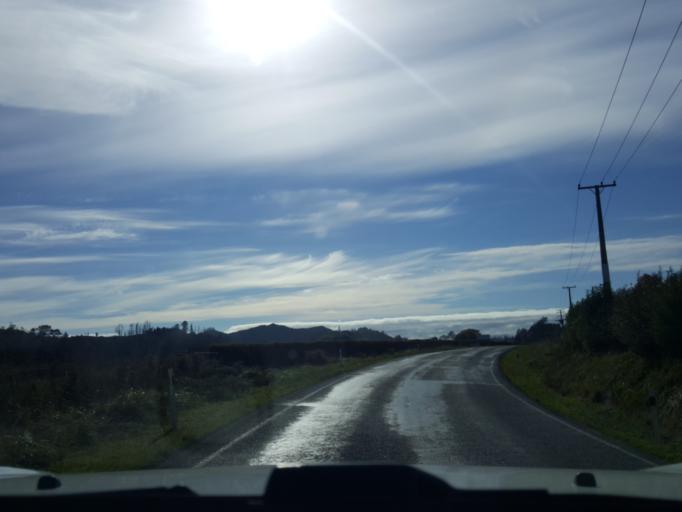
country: NZ
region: Waikato
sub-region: Waikato District
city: Ngaruawahia
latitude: -37.6058
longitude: 175.1983
